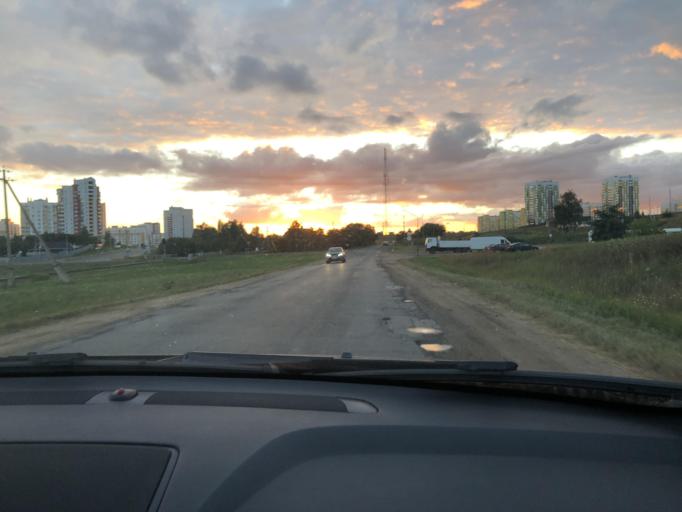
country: BY
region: Grodnenskaya
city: Hrodna
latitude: 53.7133
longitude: 23.8760
